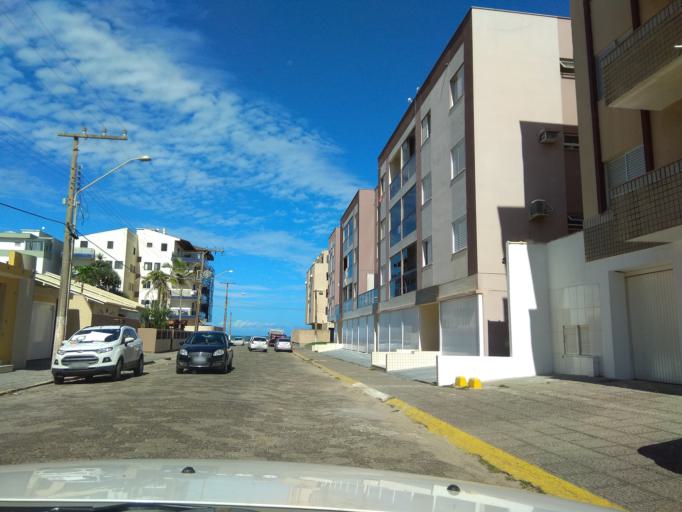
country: BR
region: Santa Catarina
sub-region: Laguna
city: Laguna
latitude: -28.4833
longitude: -48.7678
